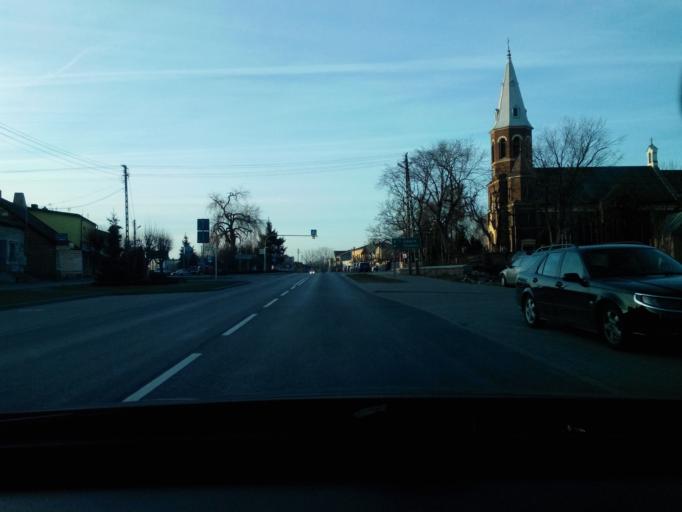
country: PL
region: Kujawsko-Pomorskie
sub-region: Powiat wloclawski
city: Lubien Kujawski
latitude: 52.4042
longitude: 19.1671
